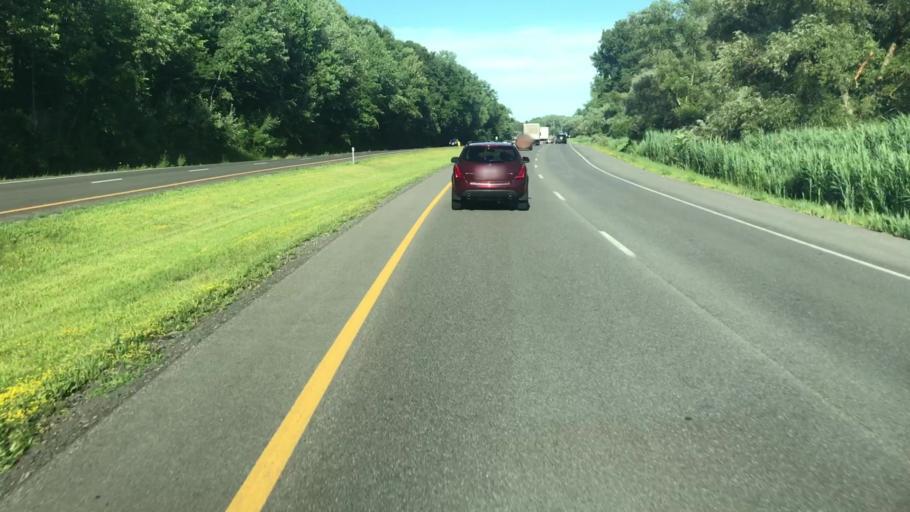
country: US
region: New York
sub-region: Onondaga County
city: Liverpool
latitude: 43.1315
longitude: -76.2303
